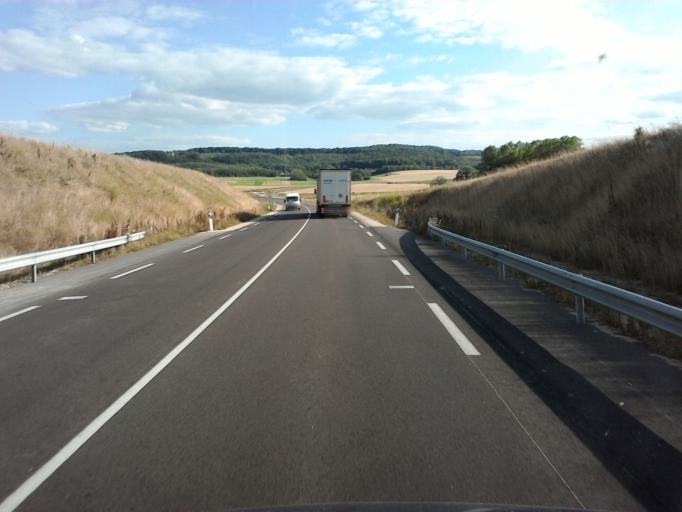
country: FR
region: Franche-Comte
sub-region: Departement de la Haute-Saone
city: Frotey-les-Vesoul
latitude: 47.6914
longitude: 6.2664
